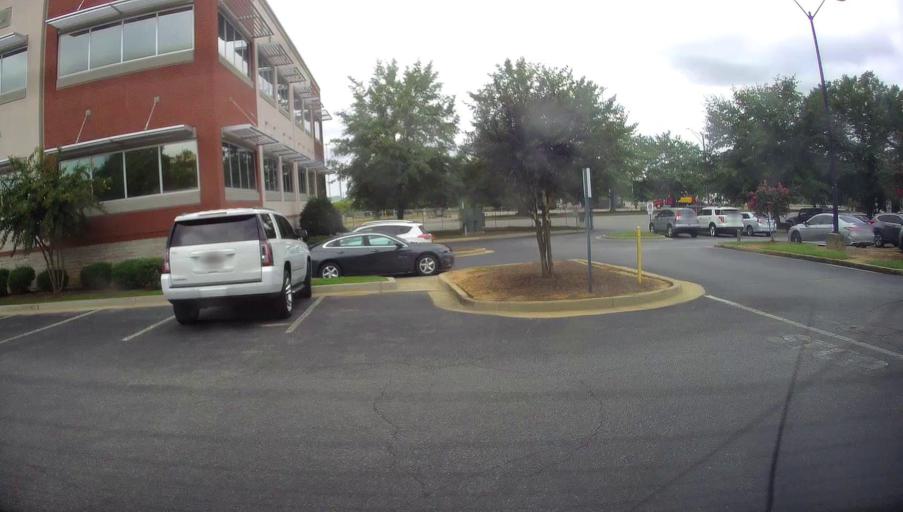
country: US
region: Georgia
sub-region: Bibb County
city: Macon
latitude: 32.8452
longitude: -83.6188
